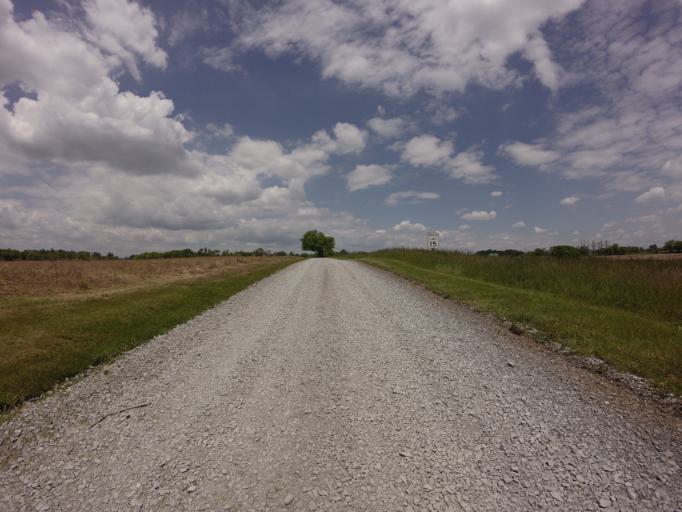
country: US
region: Maryland
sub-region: Frederick County
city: Ballenger Creek
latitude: 39.3709
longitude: -77.3986
